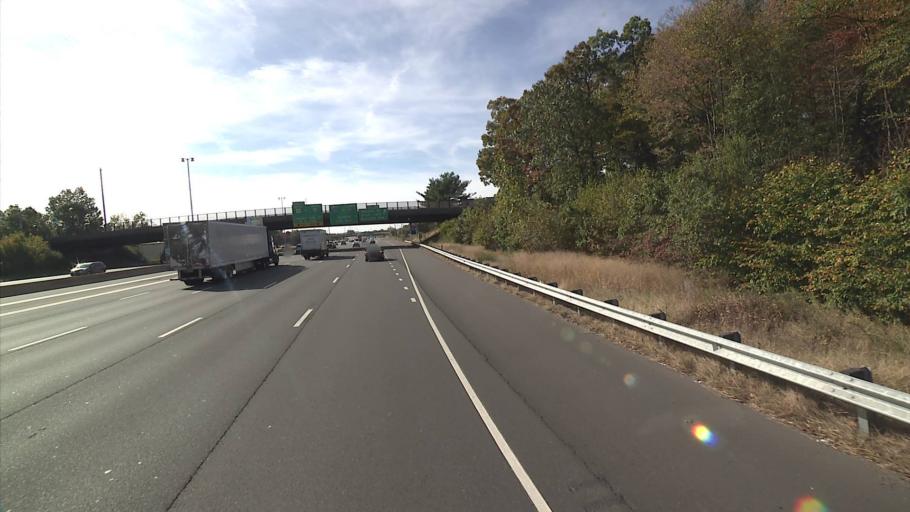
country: US
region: Connecticut
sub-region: Hartford County
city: East Hartford
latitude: 41.7681
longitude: -72.6174
